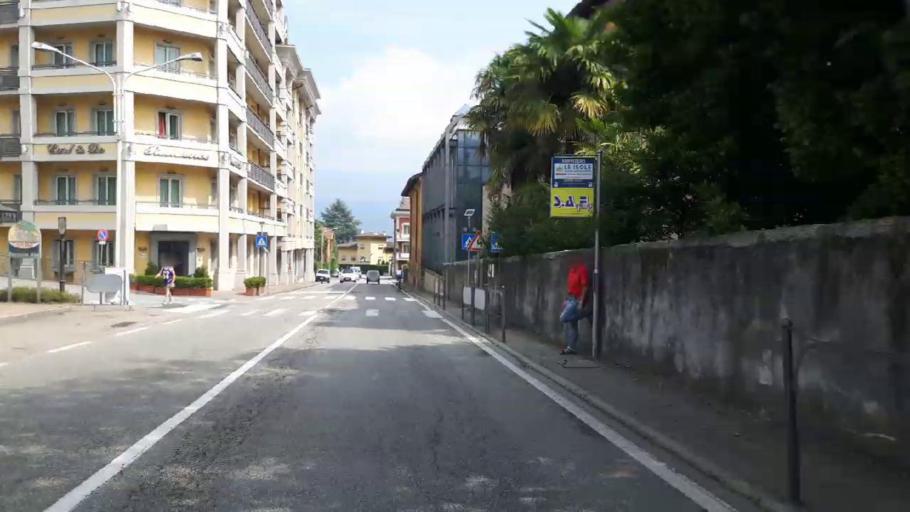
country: IT
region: Piedmont
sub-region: Provincia Verbano-Cusio-Ossola
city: Baveno
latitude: 45.9138
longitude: 8.5017
